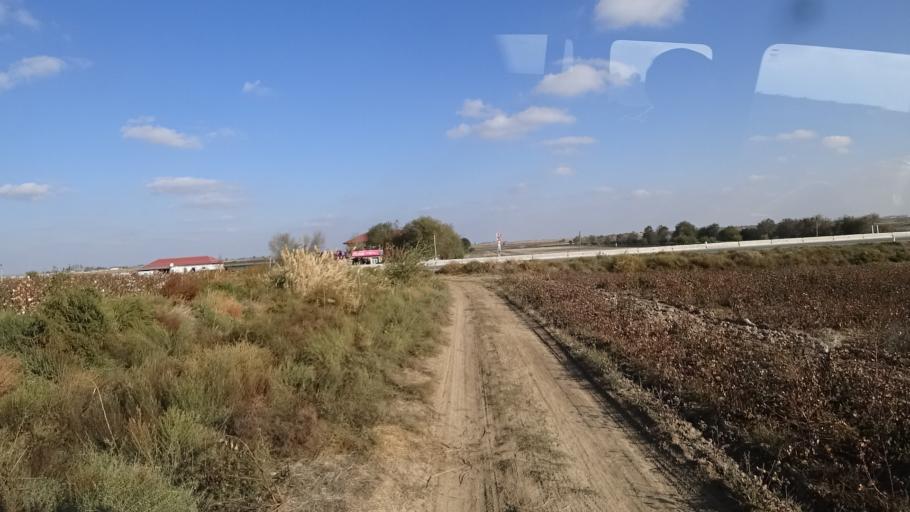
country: UZ
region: Jizzax
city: Jizzax
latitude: 40.1363
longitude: 67.9530
